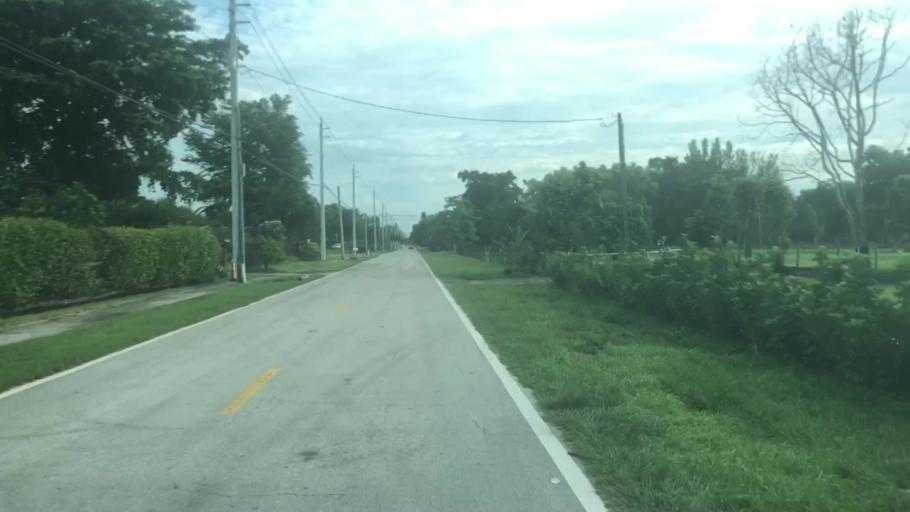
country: US
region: Florida
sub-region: Broward County
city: Southwest Ranches
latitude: 26.0919
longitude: -80.3342
